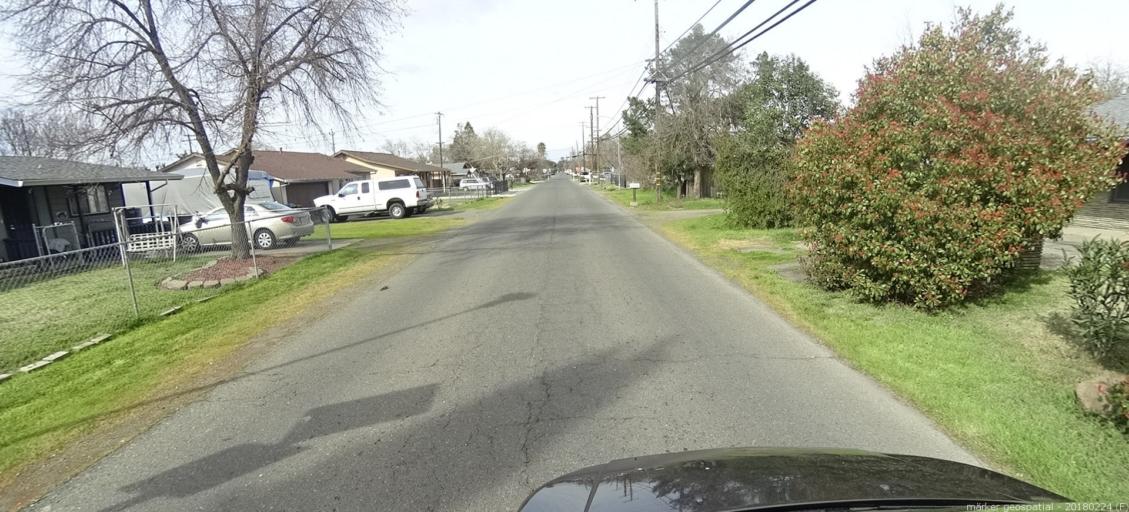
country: US
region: California
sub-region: Sacramento County
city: Rio Linda
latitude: 38.6971
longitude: -121.4476
